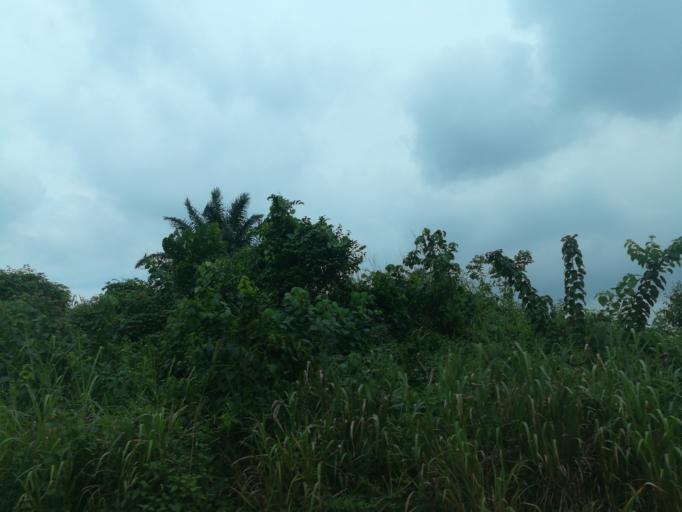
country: NG
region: Lagos
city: Ejirin
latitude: 6.6471
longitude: 3.7325
